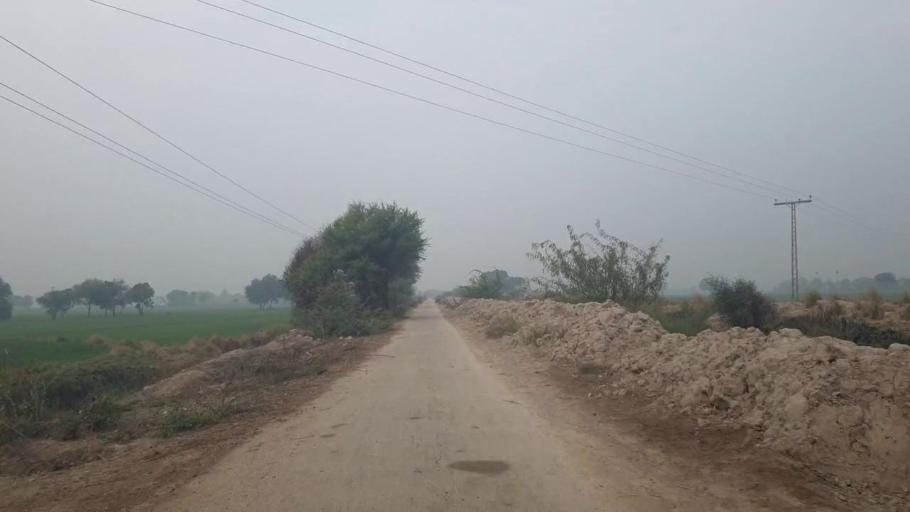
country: PK
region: Sindh
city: Tando Adam
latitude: 25.6899
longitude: 68.6610
